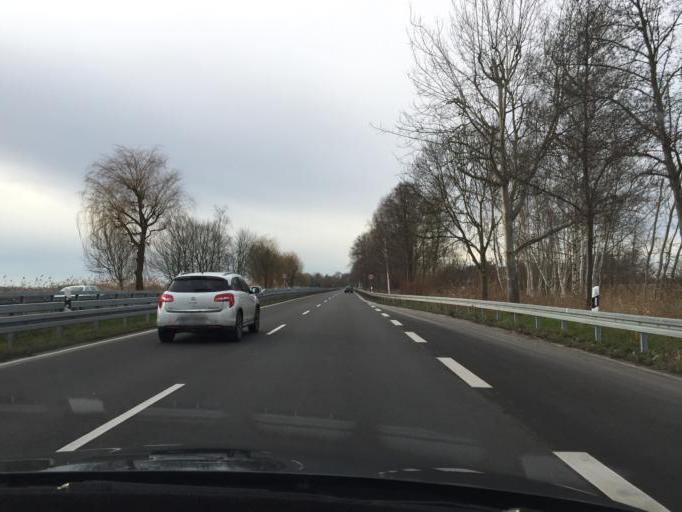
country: DE
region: Brandenburg
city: Peitz
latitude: 51.8488
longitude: 14.3965
